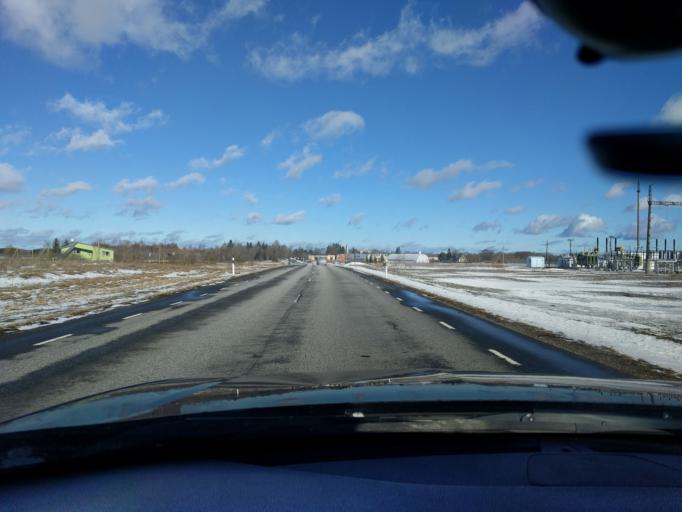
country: EE
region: Harju
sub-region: Raasiku vald
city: Raasiku
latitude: 59.3713
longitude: 25.1931
